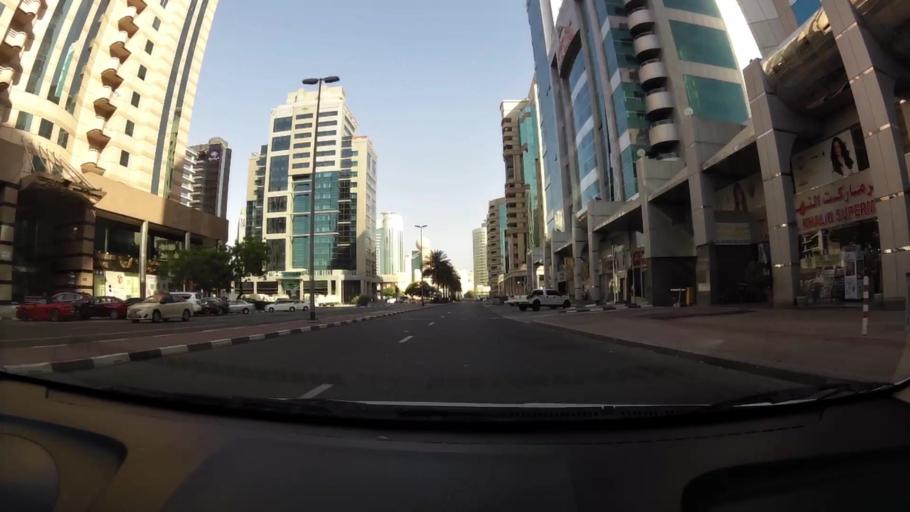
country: AE
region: Ash Shariqah
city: Sharjah
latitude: 25.2602
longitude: 55.3202
